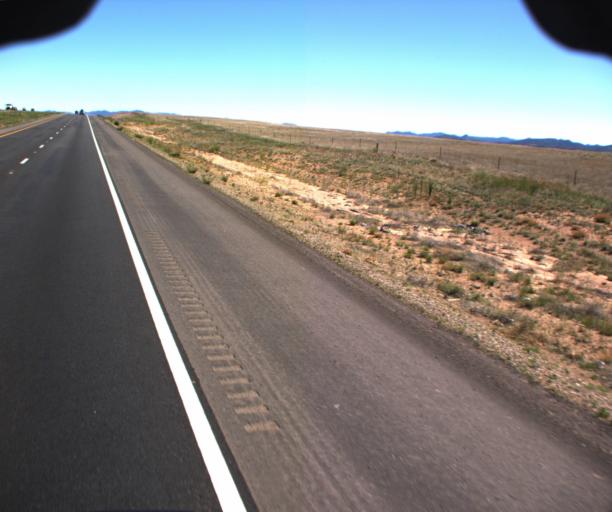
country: US
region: Arizona
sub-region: Yavapai County
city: Chino Valley
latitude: 34.6994
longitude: -112.4490
